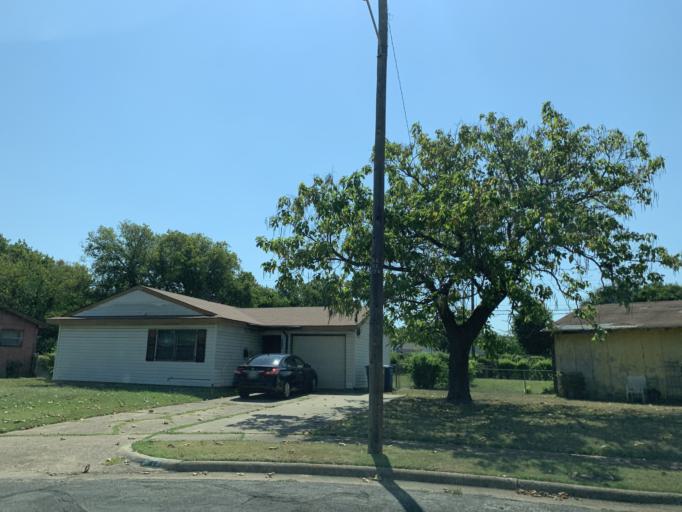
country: US
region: Texas
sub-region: Dallas County
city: Hutchins
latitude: 32.6744
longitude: -96.7582
